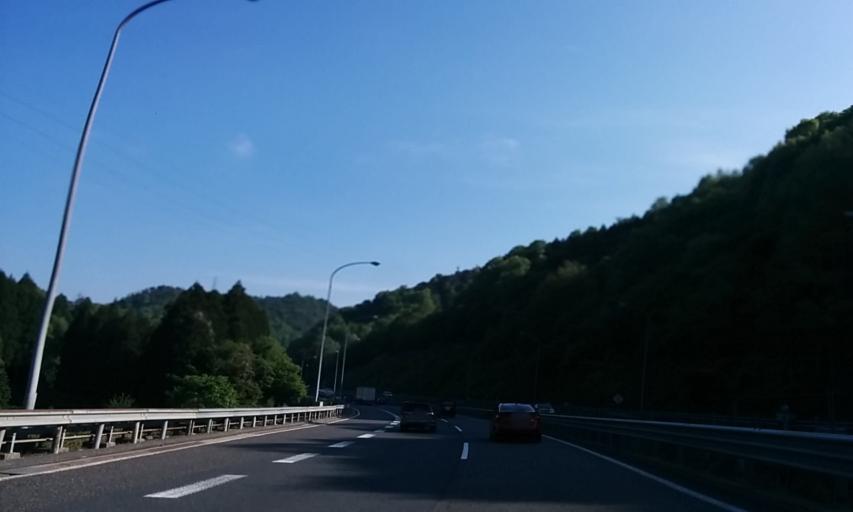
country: JP
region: Shiga Prefecture
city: Hikone
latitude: 35.2898
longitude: 136.2978
